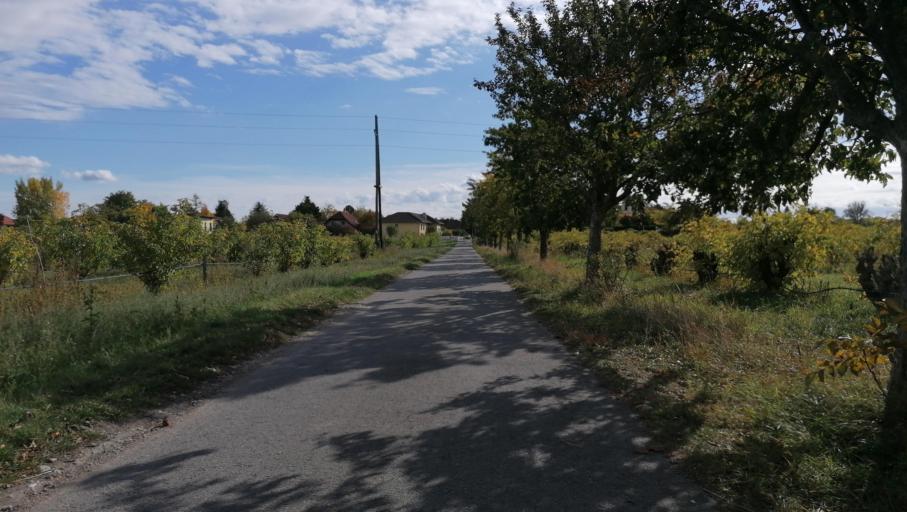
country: AT
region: Lower Austria
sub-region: Politischer Bezirk Baden
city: Tattendorf
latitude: 47.9629
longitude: 16.2972
